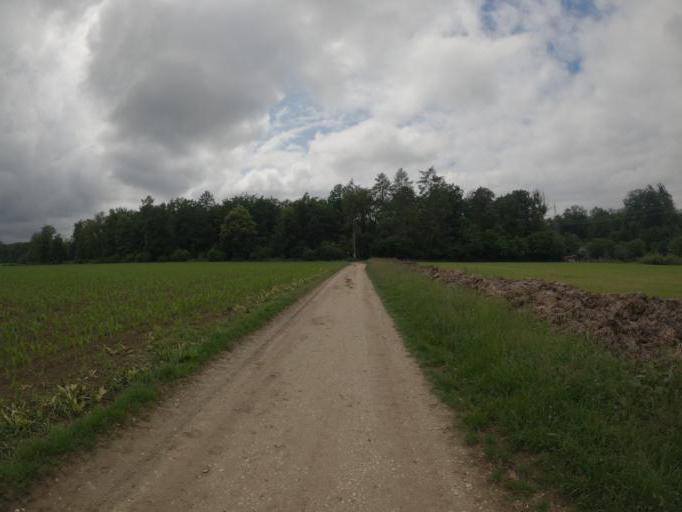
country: DE
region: Baden-Wuerttemberg
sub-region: Regierungsbezirk Stuttgart
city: Albershausen
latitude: 48.6756
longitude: 9.5515
